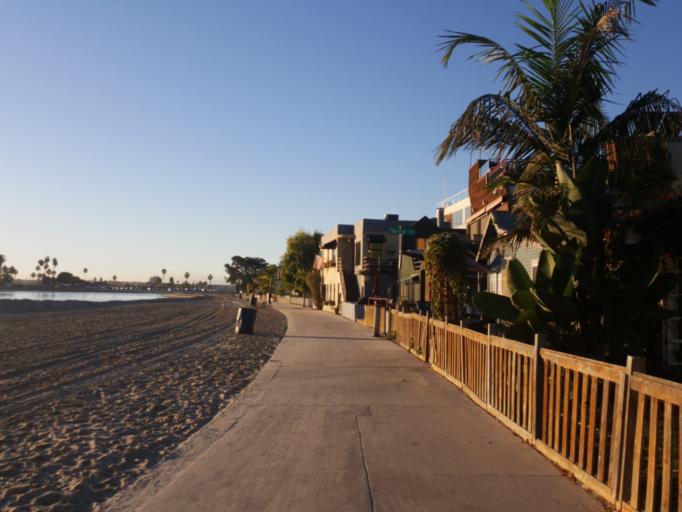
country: US
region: California
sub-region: San Diego County
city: La Jolla
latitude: 32.7871
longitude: -117.2527
